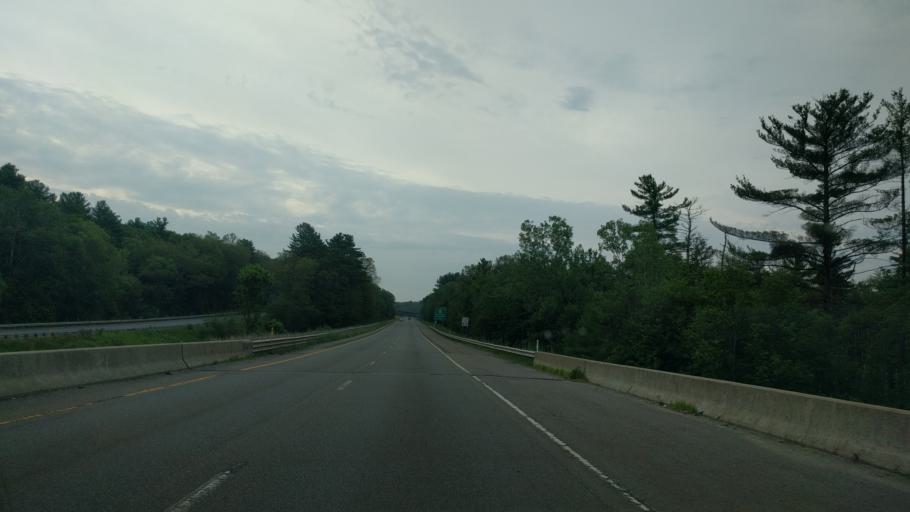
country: US
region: Massachusetts
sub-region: Worcester County
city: East Douglas
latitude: 42.0828
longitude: -71.6902
